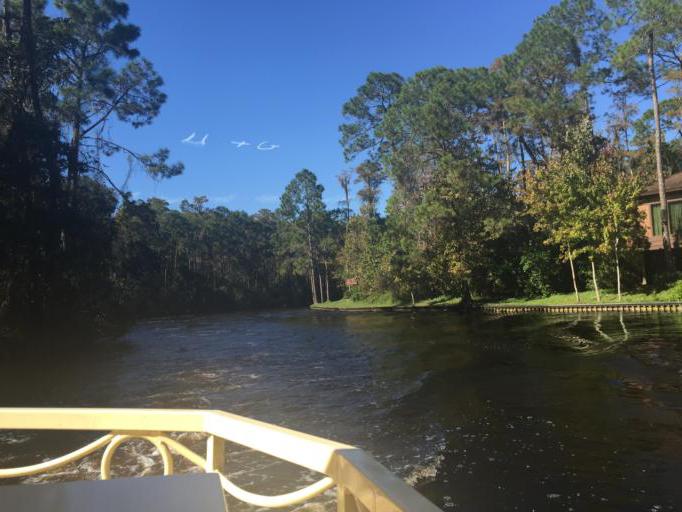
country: US
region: Florida
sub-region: Osceola County
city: Celebration
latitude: 28.3758
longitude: -81.5282
